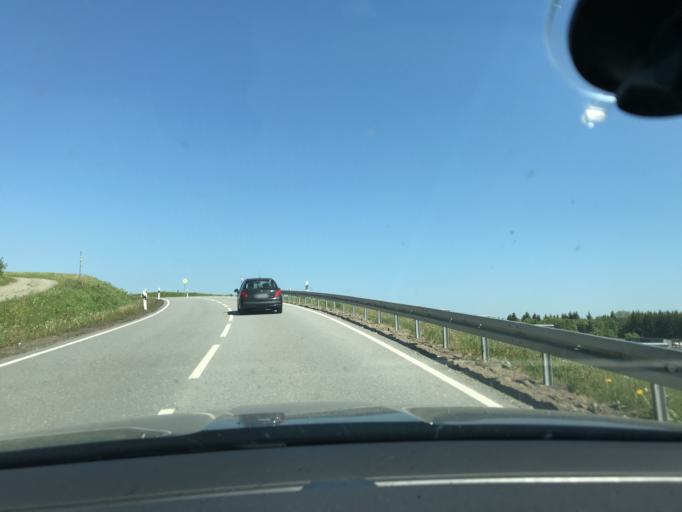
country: CZ
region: Ustecky
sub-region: Okres Chomutov
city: Vejprty
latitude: 50.4509
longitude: 13.0071
